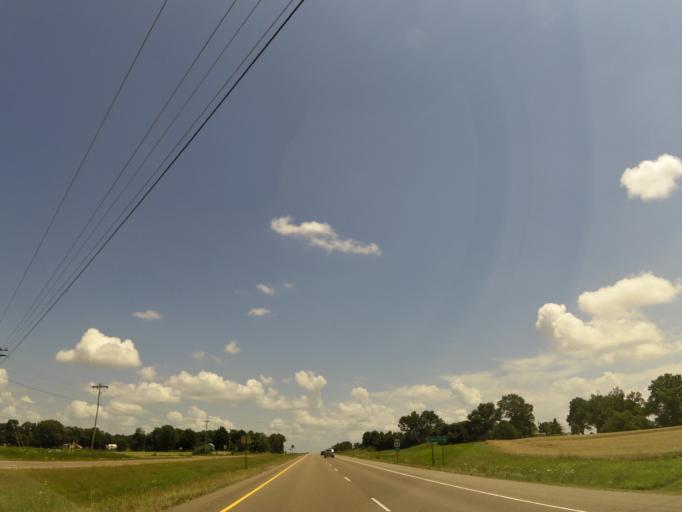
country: US
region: Tennessee
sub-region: Crockett County
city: Alamo
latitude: 35.8358
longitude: -89.1850
